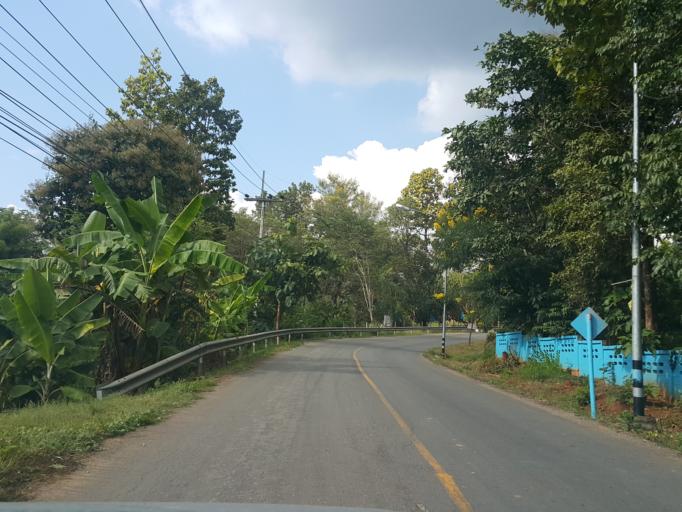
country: TH
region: Chiang Mai
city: Mae Chaem
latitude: 18.5235
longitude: 98.3627
